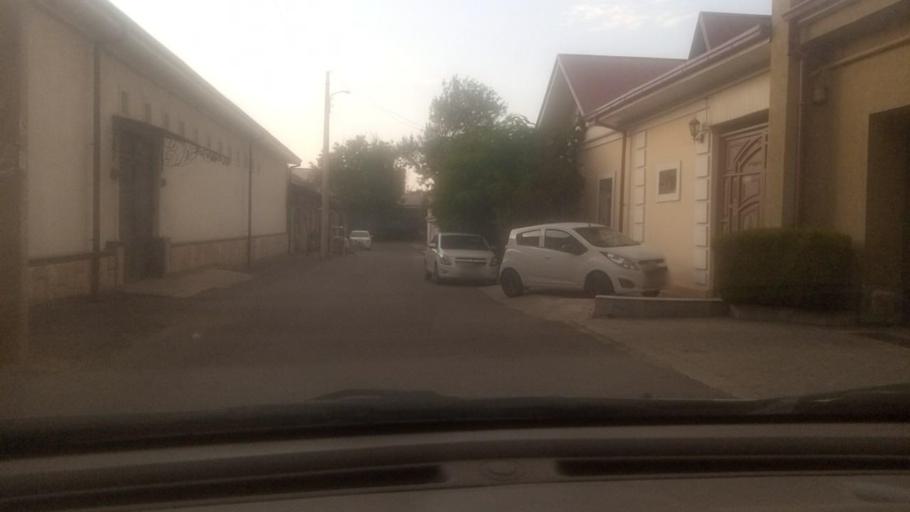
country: UZ
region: Toshkent
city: Salor
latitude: 41.3334
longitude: 69.3574
